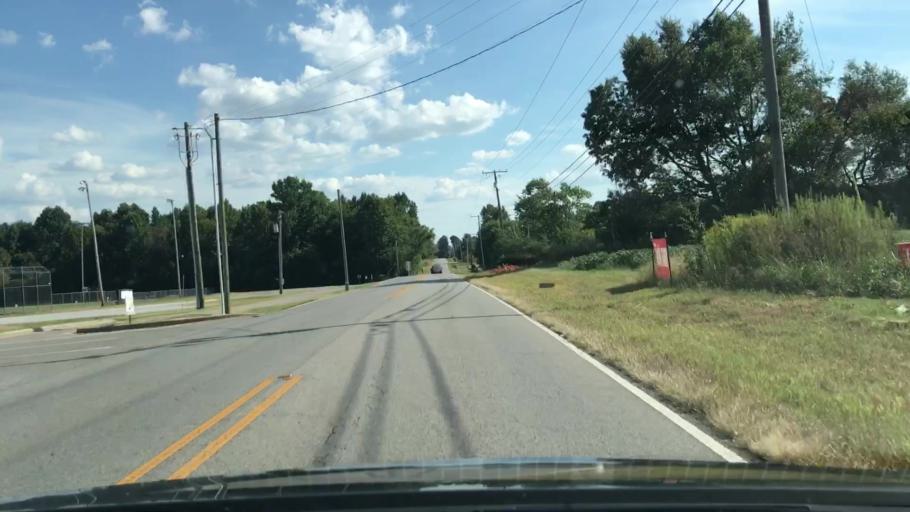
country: US
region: Alabama
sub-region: Madison County
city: Harvest
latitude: 34.8481
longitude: -86.7492
